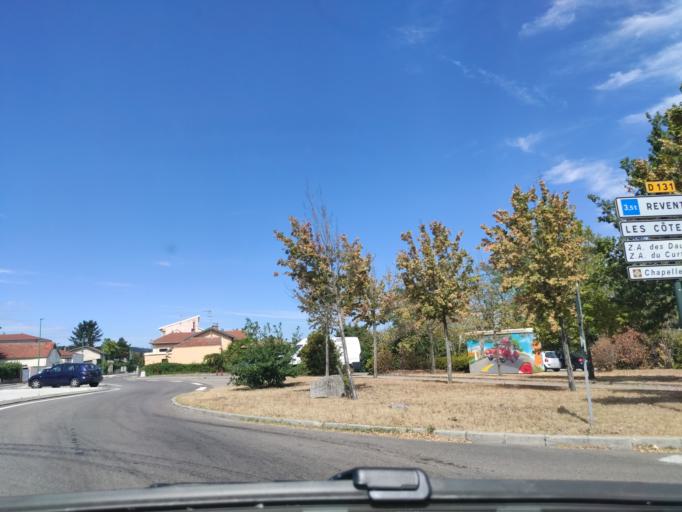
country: FR
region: Rhone-Alpes
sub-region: Departement de l'Isere
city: Reventin-Vaugris
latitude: 45.4724
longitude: 4.8292
